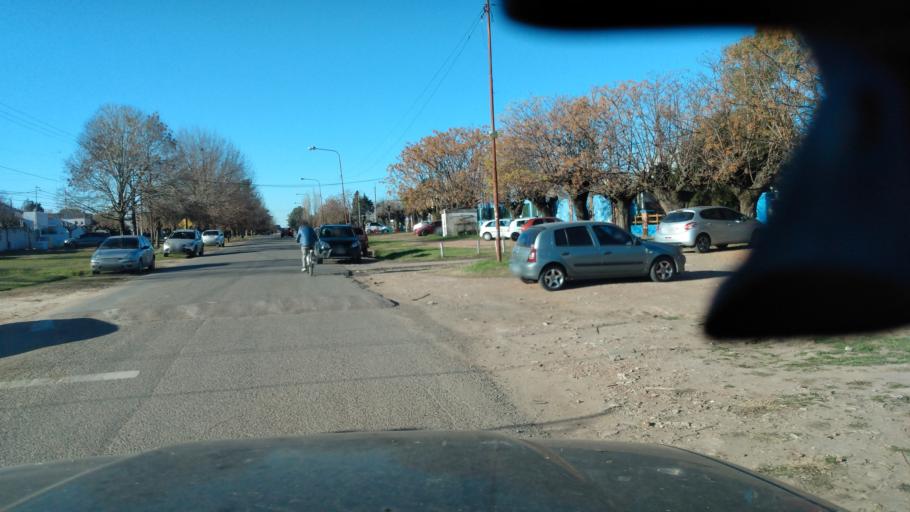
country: AR
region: Buenos Aires
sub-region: Partido de Lujan
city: Lujan
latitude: -34.5710
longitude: -59.1813
